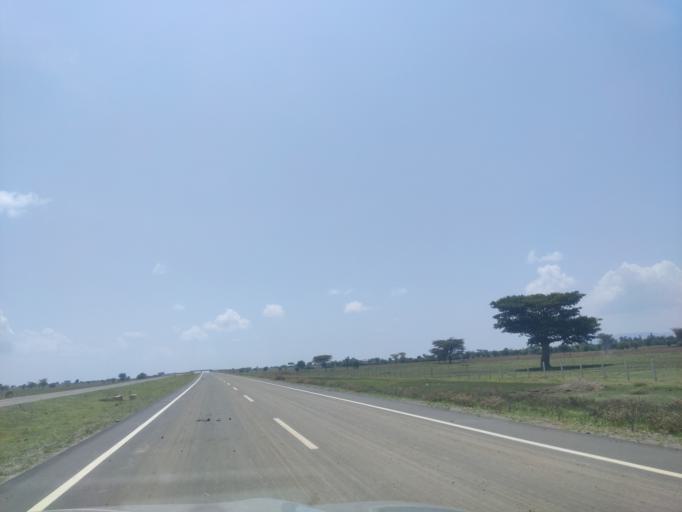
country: ET
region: Oromiya
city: Ziway
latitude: 8.2347
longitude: 38.8765
